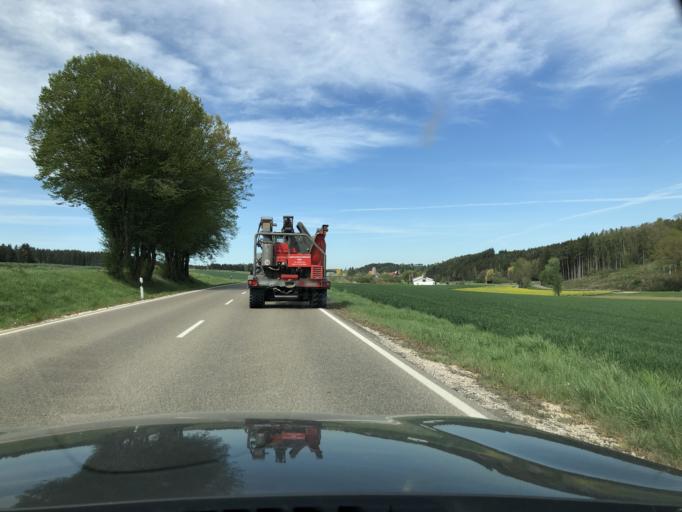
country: DE
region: Bavaria
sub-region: Swabia
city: Laugna
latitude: 48.5421
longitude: 10.7314
